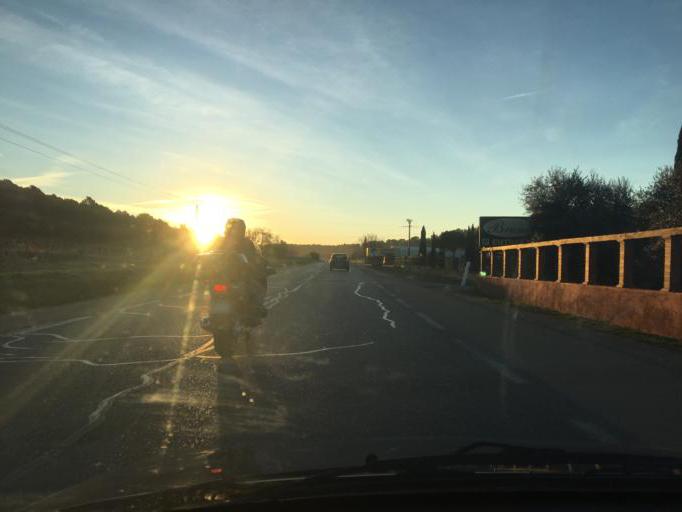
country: FR
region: Provence-Alpes-Cote d'Azur
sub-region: Departement du Var
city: Lorgues
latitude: 43.4723
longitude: 6.3792
